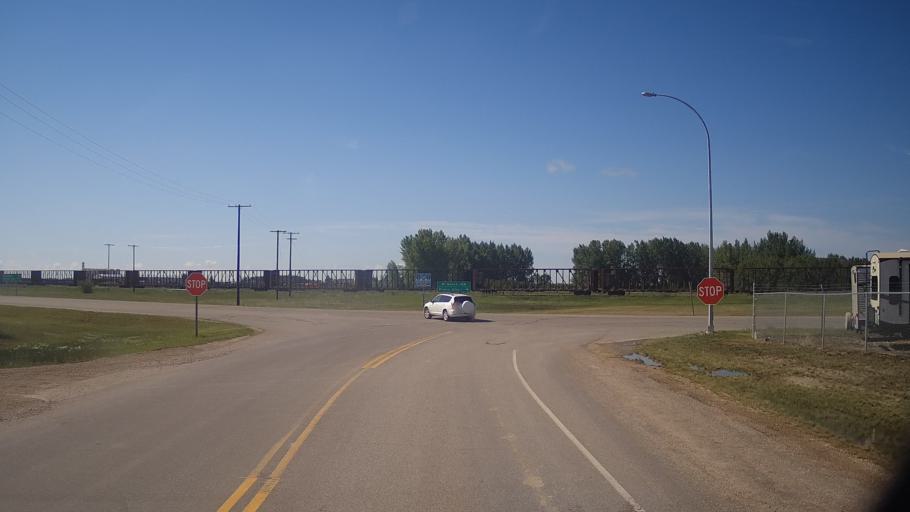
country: CA
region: Saskatchewan
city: Watrous
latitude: 51.6664
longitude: -105.4517
